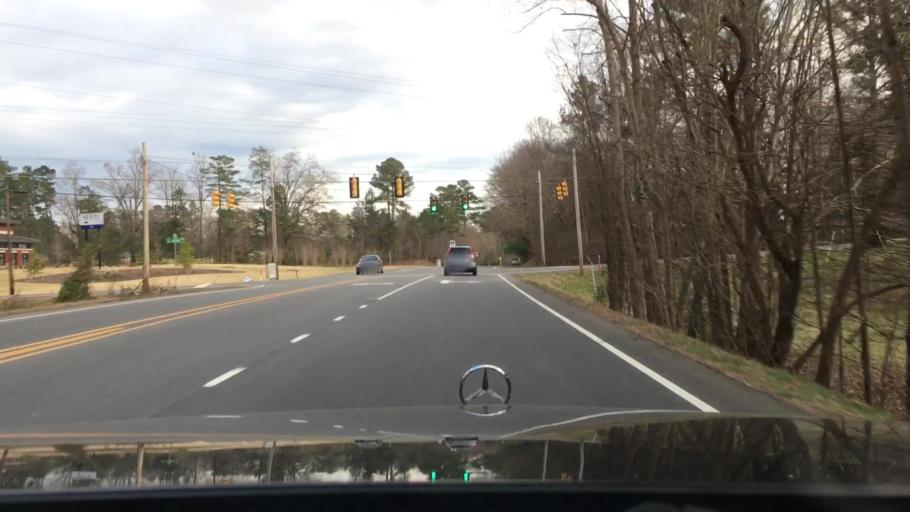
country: US
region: North Carolina
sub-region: Orange County
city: Hillsborough
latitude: 36.0837
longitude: -79.0839
